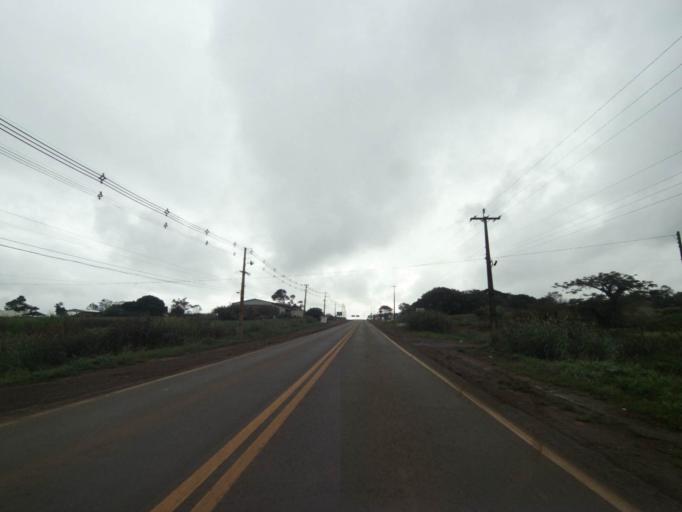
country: BR
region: Parana
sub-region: Marechal Candido Rondon
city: Marechal Candido Rondon
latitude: -24.5683
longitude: -54.0252
